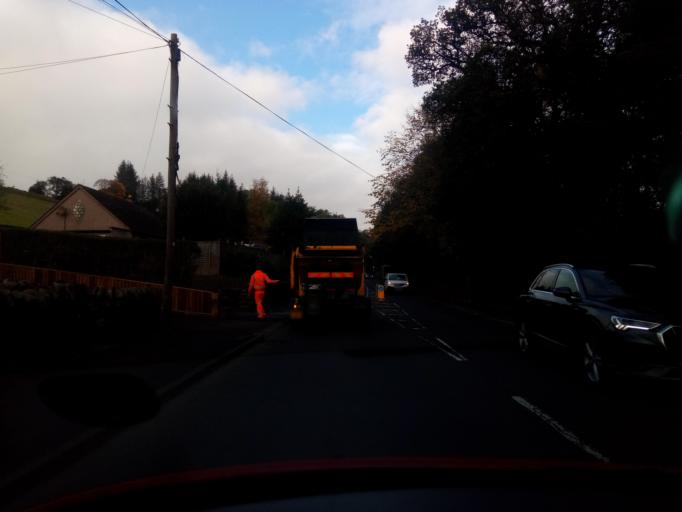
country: GB
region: Scotland
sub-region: The Scottish Borders
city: Galashiels
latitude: 55.6271
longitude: -2.8359
